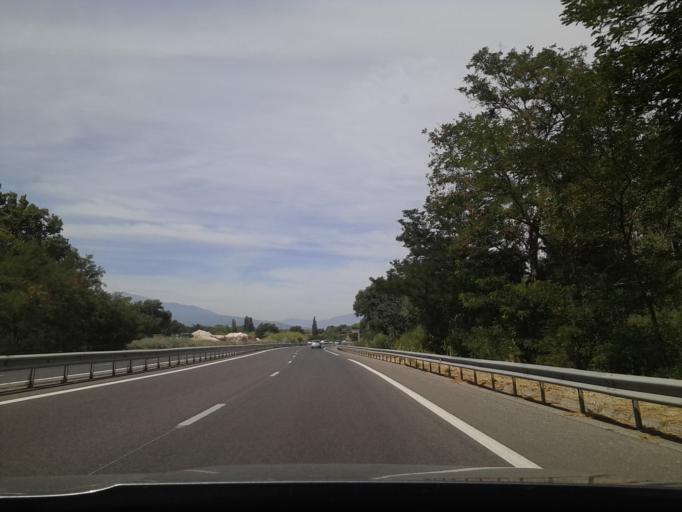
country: FR
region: Languedoc-Roussillon
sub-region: Departement des Pyrenees-Orientales
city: Saint-Esteve
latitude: 42.6938
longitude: 2.8410
